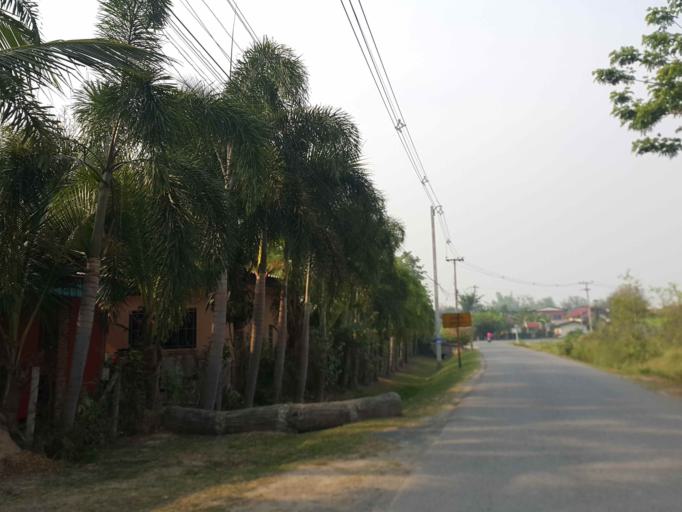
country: TH
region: Chiang Mai
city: San Kamphaeng
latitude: 18.7878
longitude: 99.0823
